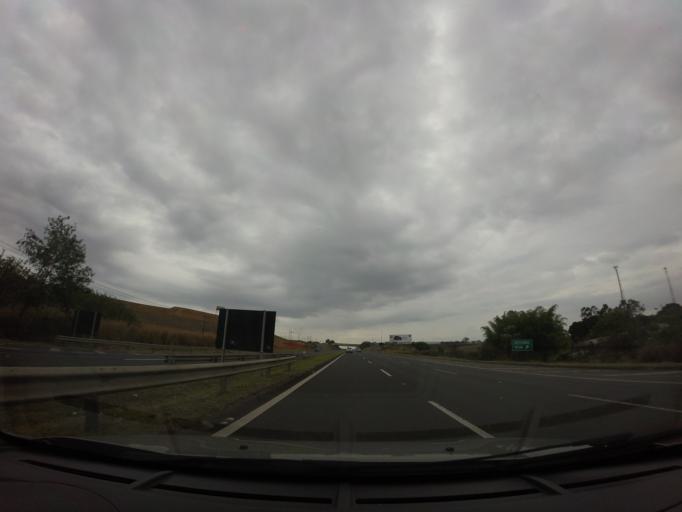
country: BR
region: Sao Paulo
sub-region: Santa Barbara D'Oeste
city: Santa Barbara d'Oeste
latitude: -22.7594
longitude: -47.4663
